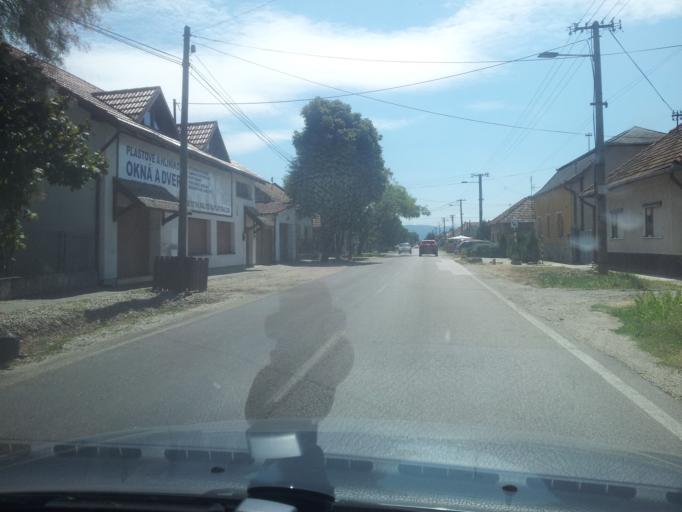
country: SK
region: Nitriansky
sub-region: Okres Nove Zamky
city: Sturovo
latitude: 47.8173
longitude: 18.6942
